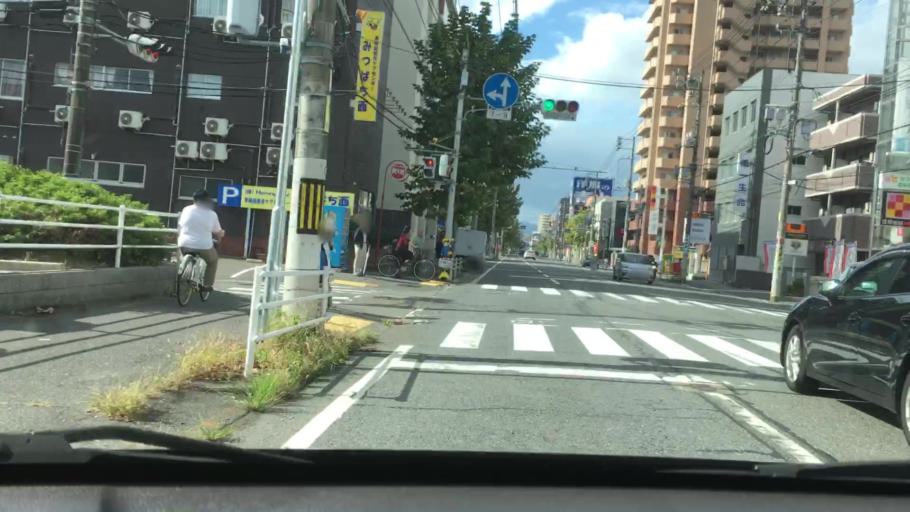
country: JP
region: Hiroshima
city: Hiroshima-shi
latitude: 34.3882
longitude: 132.4192
